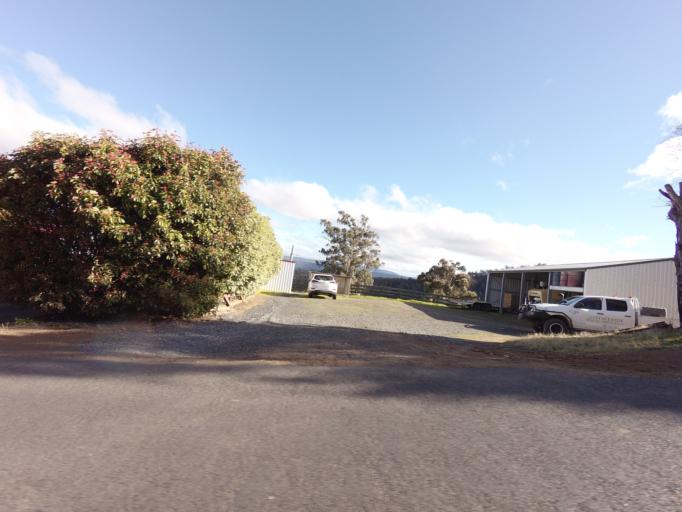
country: AU
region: Tasmania
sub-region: Derwent Valley
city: New Norfolk
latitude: -42.7210
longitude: 147.0327
